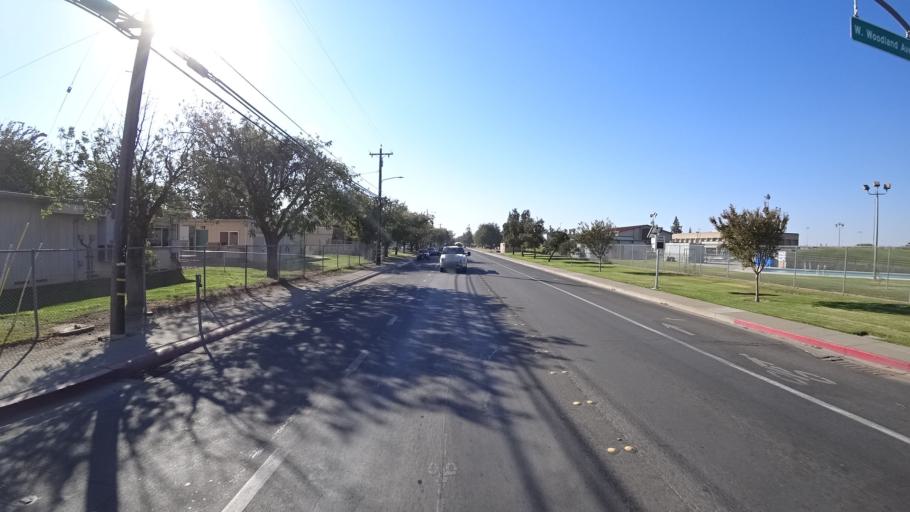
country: US
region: California
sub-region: Yolo County
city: Woodland
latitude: 38.6882
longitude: -121.7839
